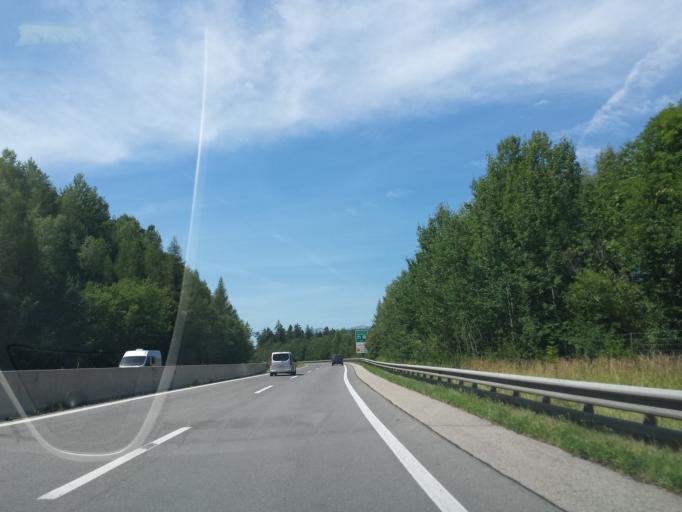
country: AT
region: Lower Austria
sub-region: Politischer Bezirk Neunkirchen
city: Raach am Hochgebirge
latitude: 47.6553
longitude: 15.9109
